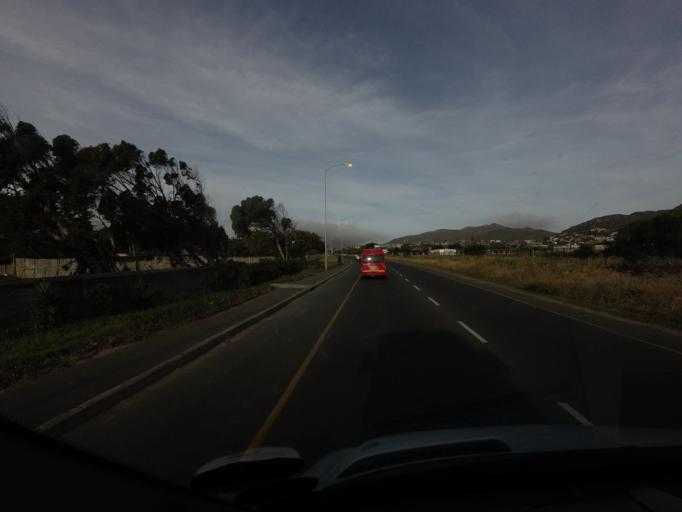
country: ZA
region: Western Cape
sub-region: City of Cape Town
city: Constantia
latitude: -34.1344
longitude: 18.3764
